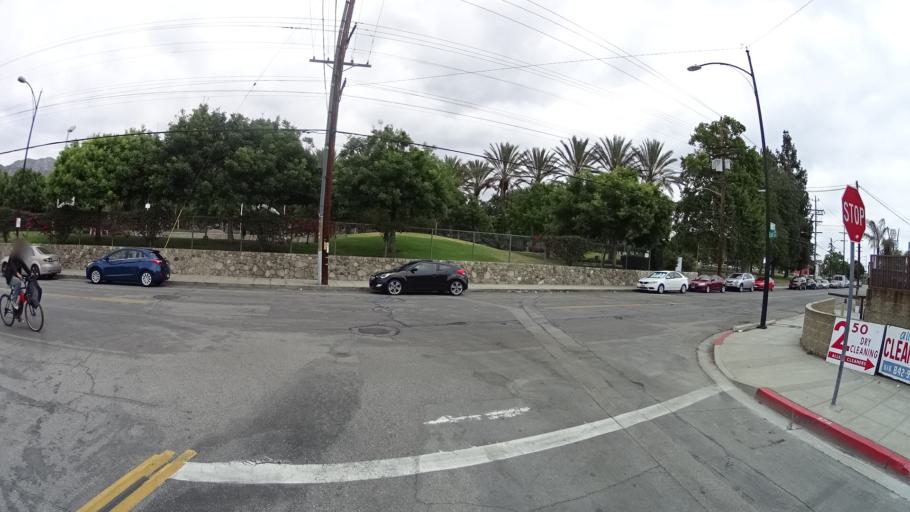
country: US
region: California
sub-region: Los Angeles County
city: Burbank
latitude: 34.1916
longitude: -118.3224
